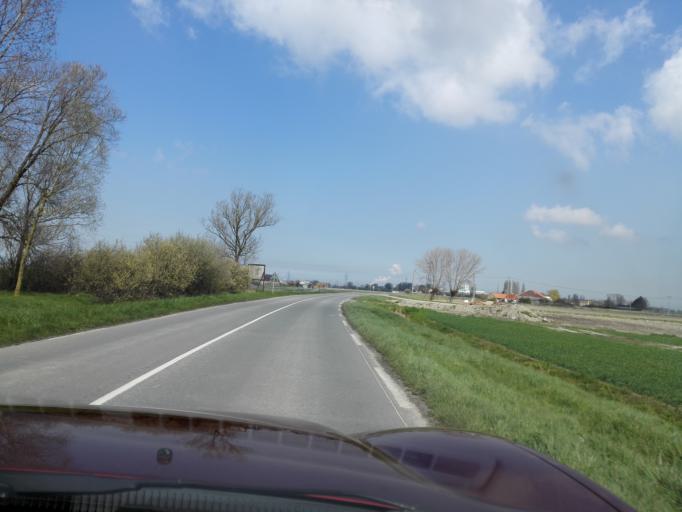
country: FR
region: Nord-Pas-de-Calais
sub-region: Departement du Nord
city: Brouckerque
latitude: 50.9611
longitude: 2.2736
